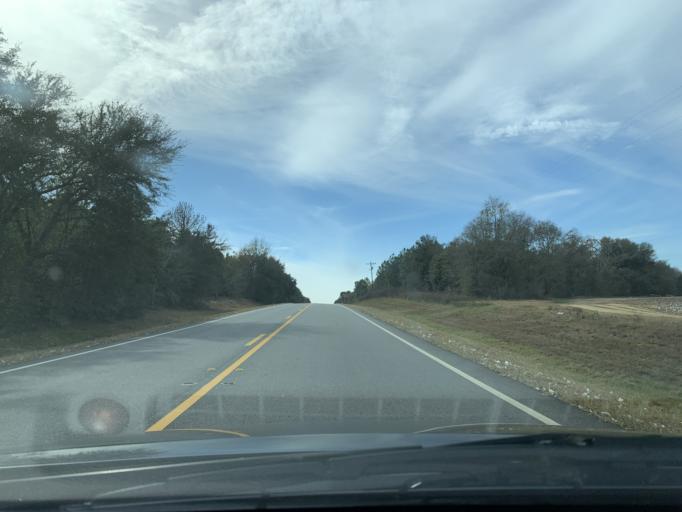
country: US
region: Georgia
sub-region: Turner County
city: Ashburn
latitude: 31.7607
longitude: -83.5445
